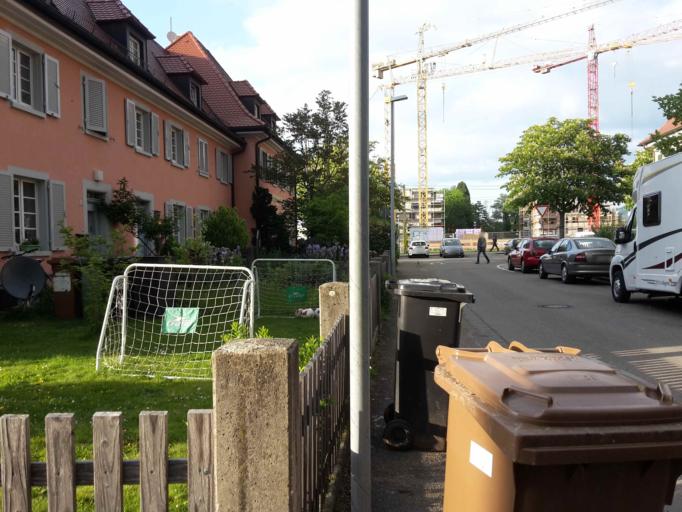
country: DE
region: Baden-Wuerttemberg
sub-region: Freiburg Region
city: Merzhausen
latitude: 47.9877
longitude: 7.8265
